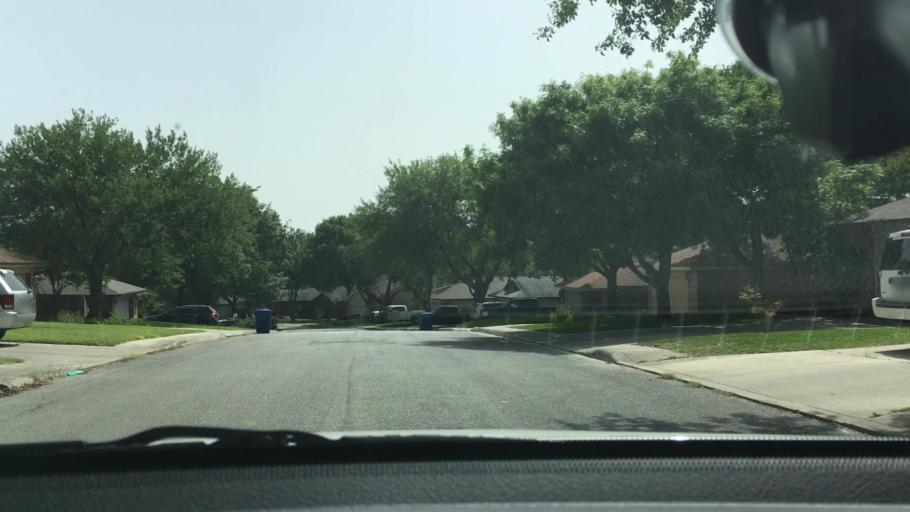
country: US
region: Texas
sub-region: Bexar County
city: Live Oak
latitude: 29.5817
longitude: -98.3779
